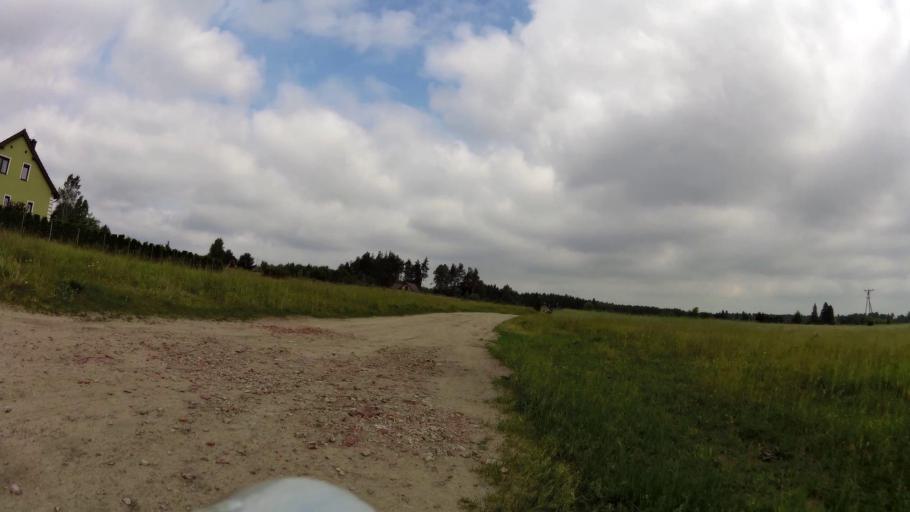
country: PL
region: West Pomeranian Voivodeship
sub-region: Powiat szczecinecki
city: Bialy Bor
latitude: 53.8941
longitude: 16.8268
